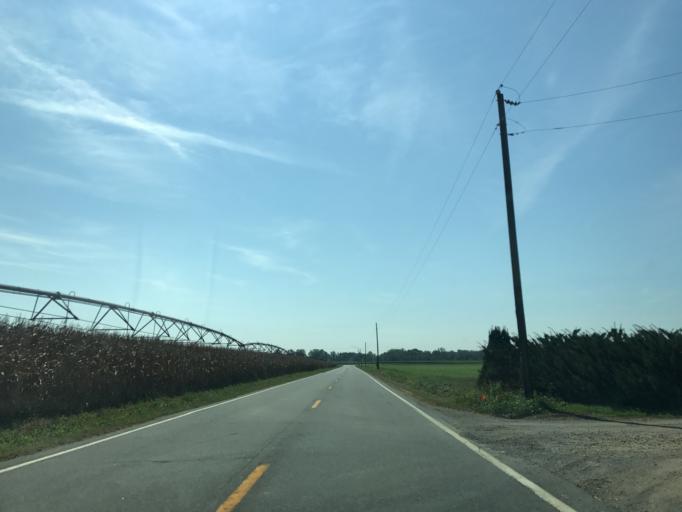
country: US
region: Maryland
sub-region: Queen Anne's County
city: Kingstown
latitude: 39.2663
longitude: -75.9145
